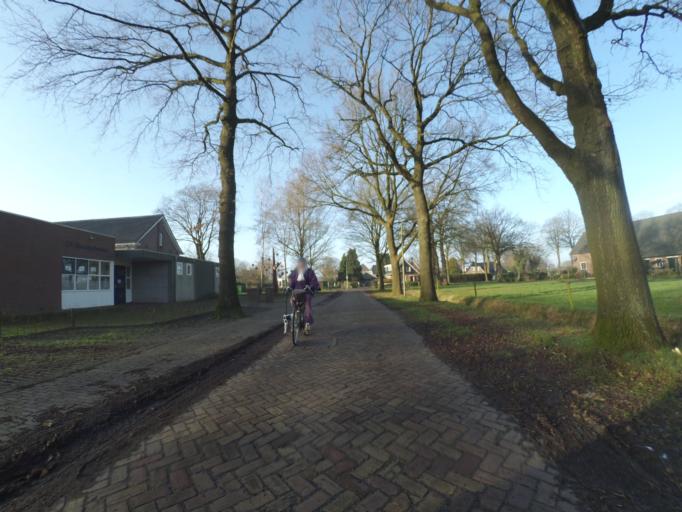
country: NL
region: Drenthe
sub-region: Gemeente Assen
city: Assen
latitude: 52.8808
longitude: 6.6468
